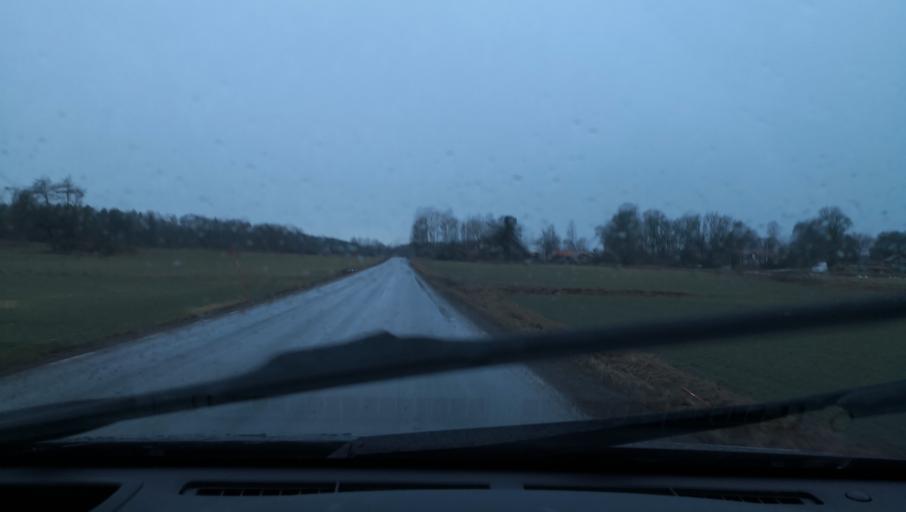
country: SE
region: Soedermanland
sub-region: Eskilstuna Kommun
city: Arla
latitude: 59.3925
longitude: 16.6593
